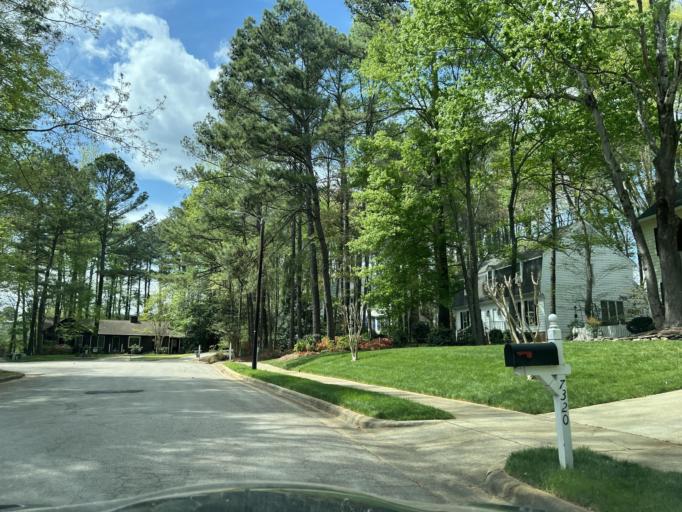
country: US
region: North Carolina
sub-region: Wake County
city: West Raleigh
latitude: 35.8854
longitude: -78.6246
